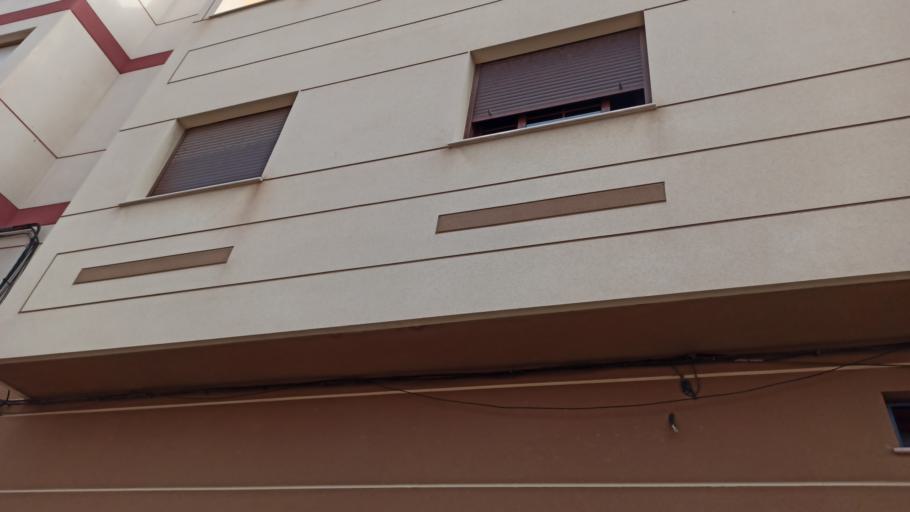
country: ES
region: Melilla
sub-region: Melilla
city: Melilla
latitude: 35.2829
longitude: -2.9469
